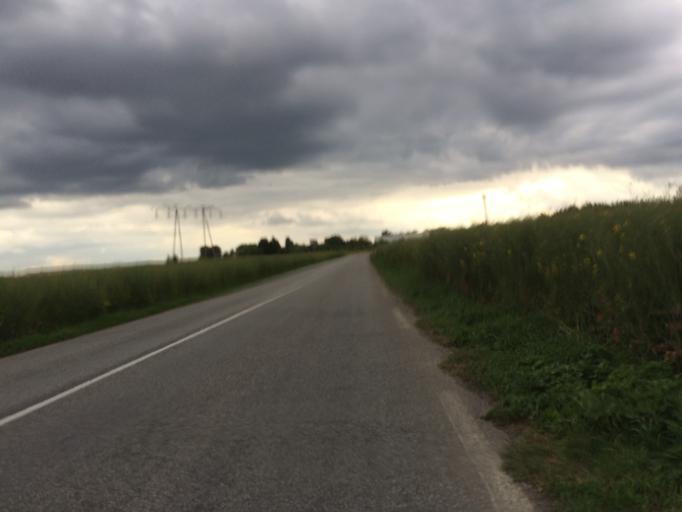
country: FR
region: Ile-de-France
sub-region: Departement de l'Essonne
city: Le Plessis-Pate
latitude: 48.6183
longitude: 2.3429
